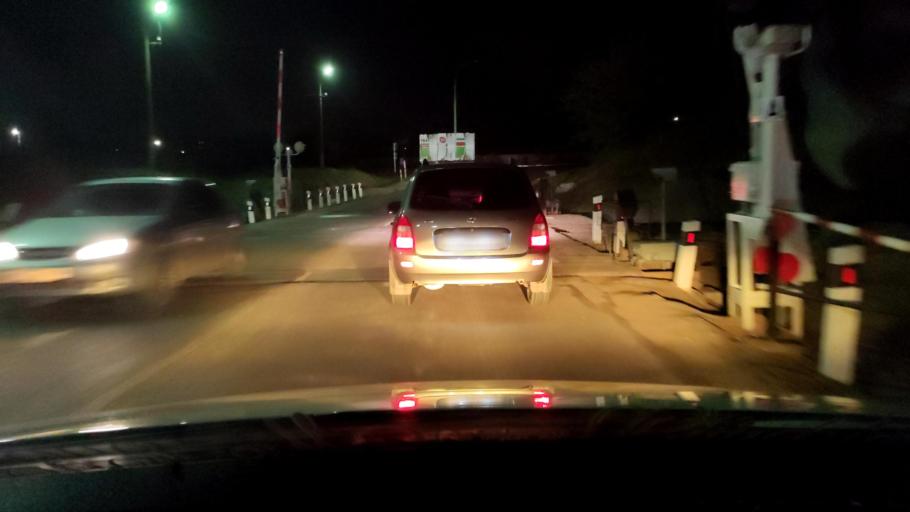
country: RU
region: Voronezj
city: Semiluki
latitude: 51.6804
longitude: 39.0233
